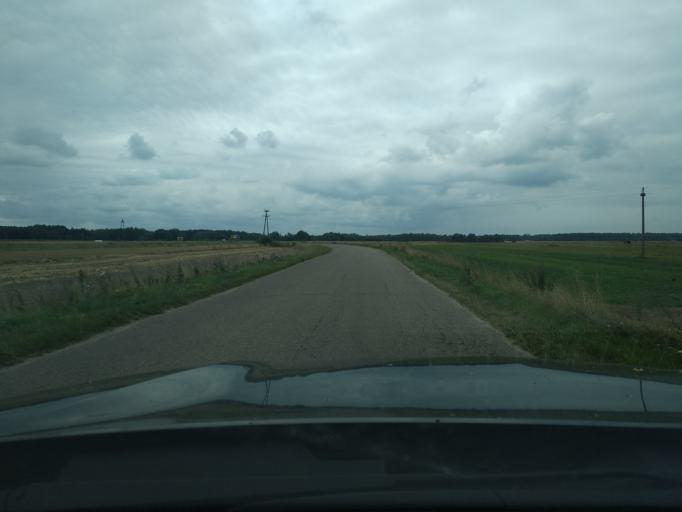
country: PL
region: Masovian Voivodeship
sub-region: Powiat pultuski
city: Obryte
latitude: 52.7532
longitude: 21.2164
